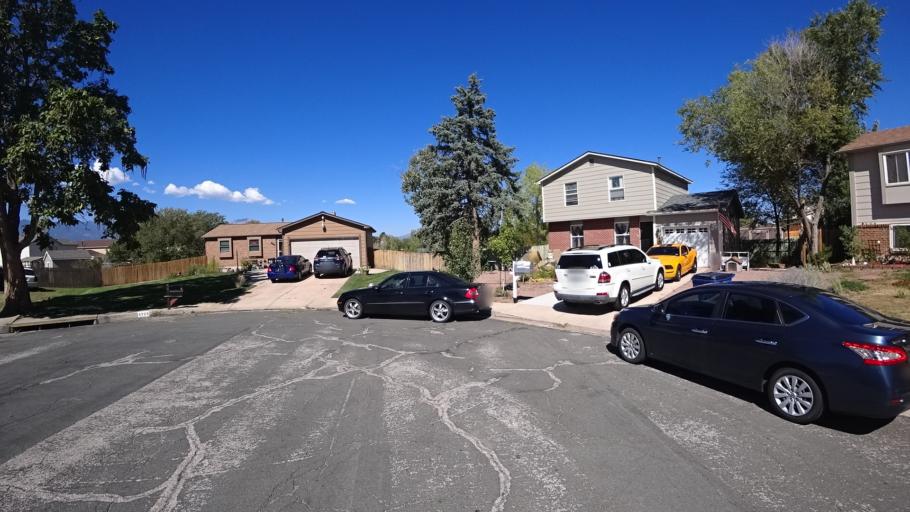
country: US
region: Colorado
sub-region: El Paso County
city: Stratmoor
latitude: 38.8141
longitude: -104.7420
